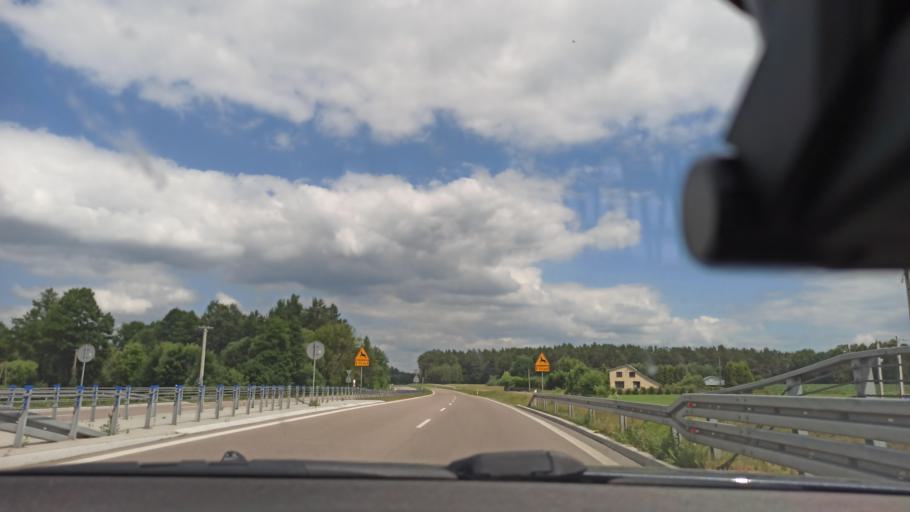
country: PL
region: Podlasie
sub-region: Powiat bialostocki
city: Suraz
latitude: 53.0145
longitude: 22.9706
